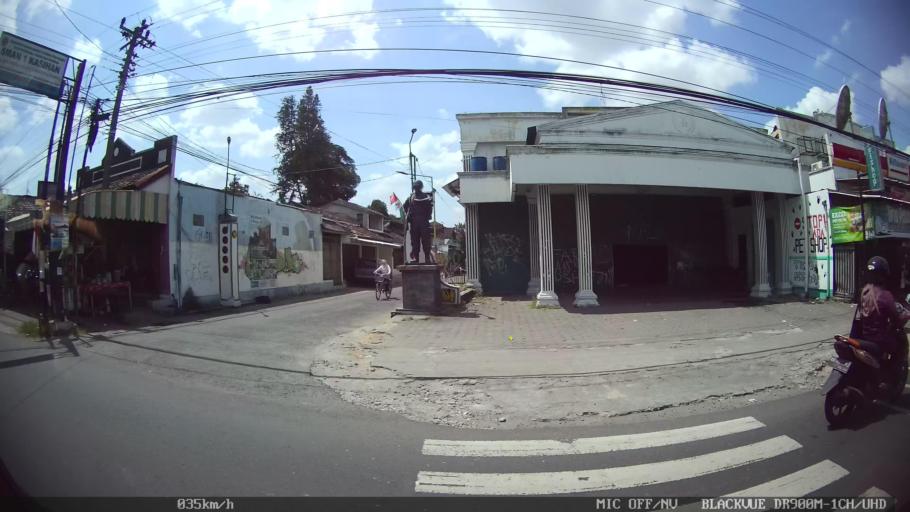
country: ID
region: Daerah Istimewa Yogyakarta
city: Kasihan
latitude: -7.8183
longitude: 110.3483
